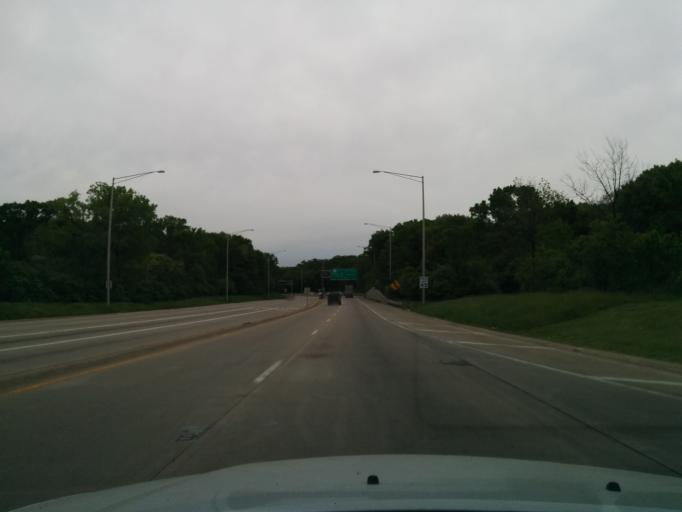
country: US
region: Illinois
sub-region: Cook County
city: Willow Springs
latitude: 41.7325
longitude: -87.8523
